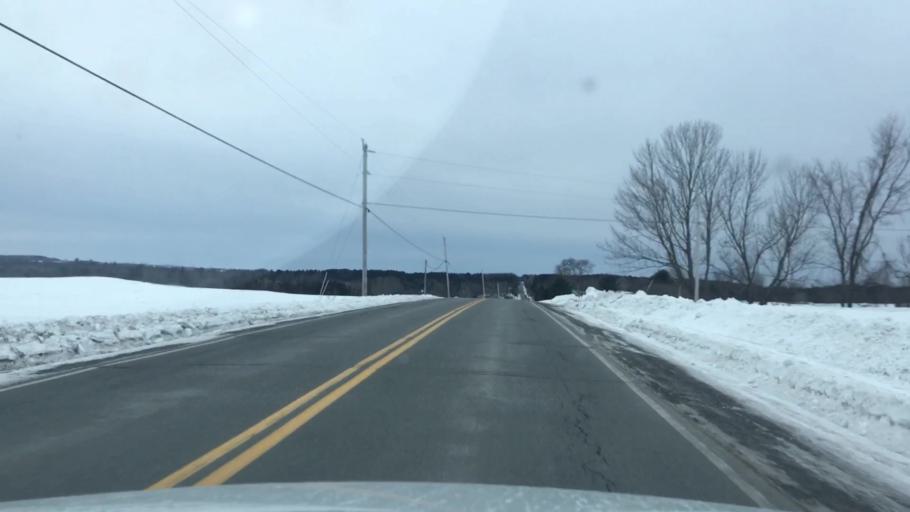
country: US
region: Maine
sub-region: Penobscot County
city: Garland
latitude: 44.9665
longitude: -69.1678
